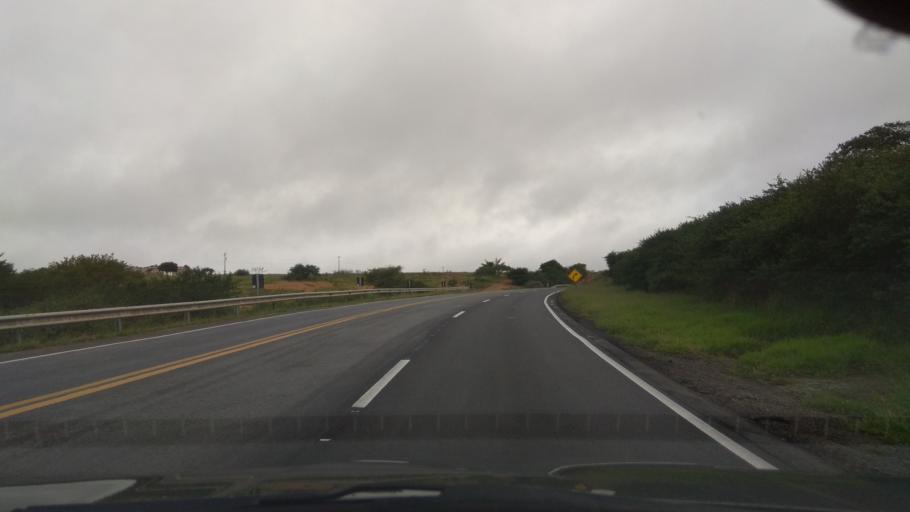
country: BR
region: Bahia
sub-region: Santa Ines
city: Santa Ines
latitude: -13.0601
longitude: -39.9568
